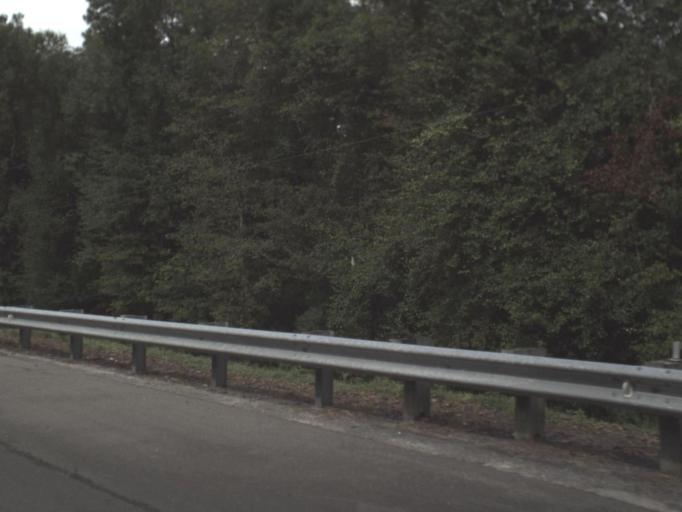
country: US
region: Florida
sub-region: Columbia County
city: Five Points
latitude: 30.2662
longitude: -82.6360
